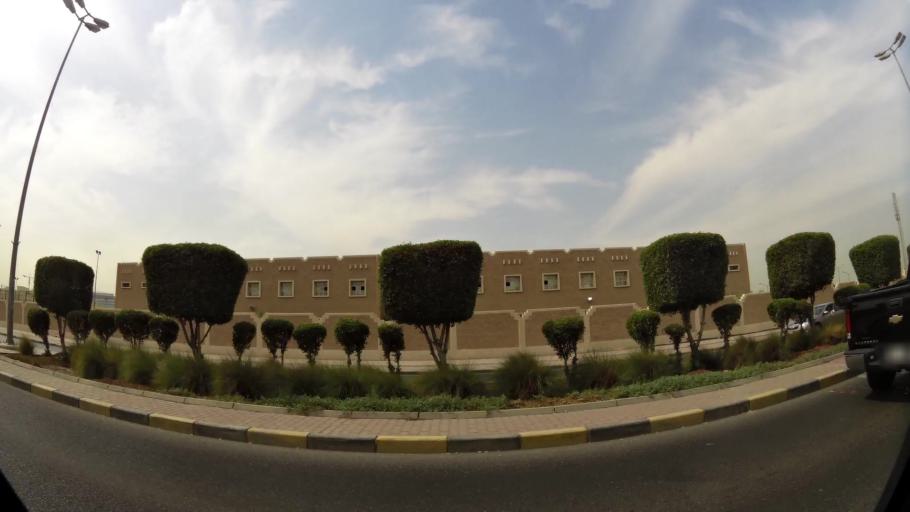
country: KW
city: Bayan
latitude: 29.2842
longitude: 48.0203
